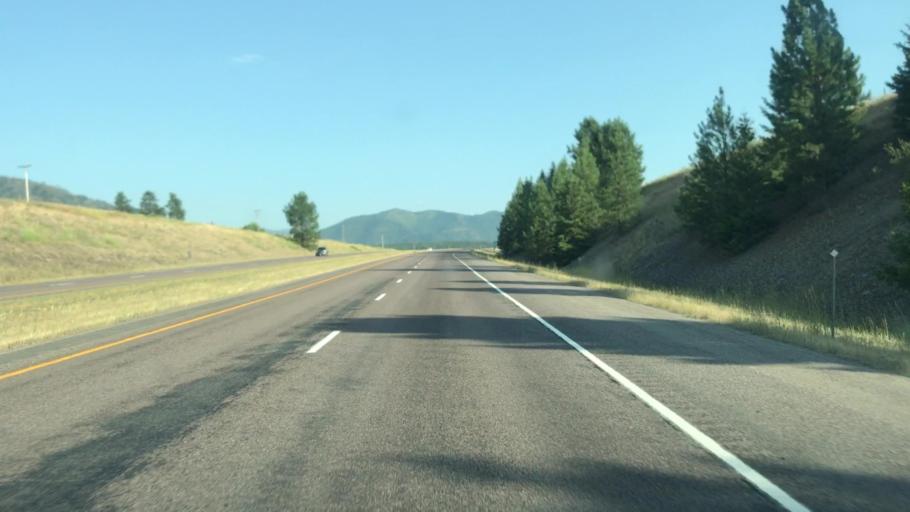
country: US
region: Montana
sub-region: Mineral County
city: Superior
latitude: 47.0498
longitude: -114.7557
